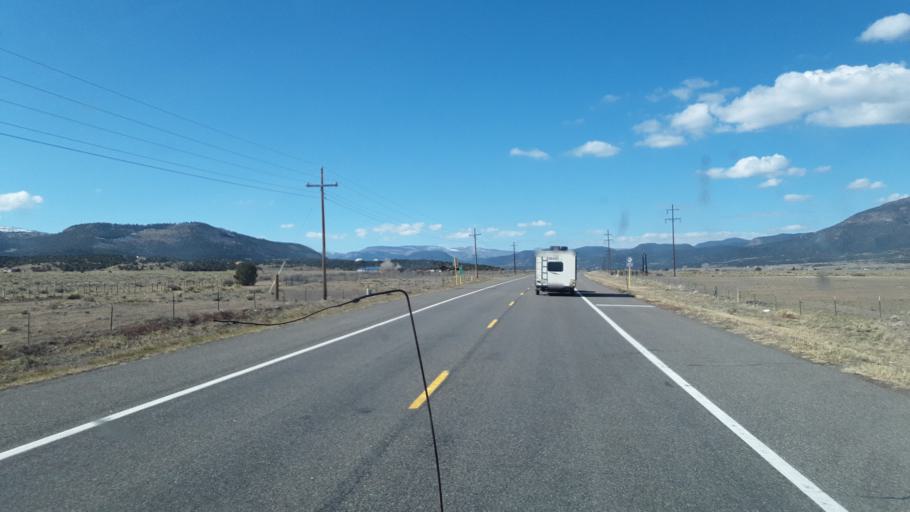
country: US
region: Colorado
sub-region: Rio Grande County
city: Del Norte
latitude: 37.6774
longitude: -106.4976
